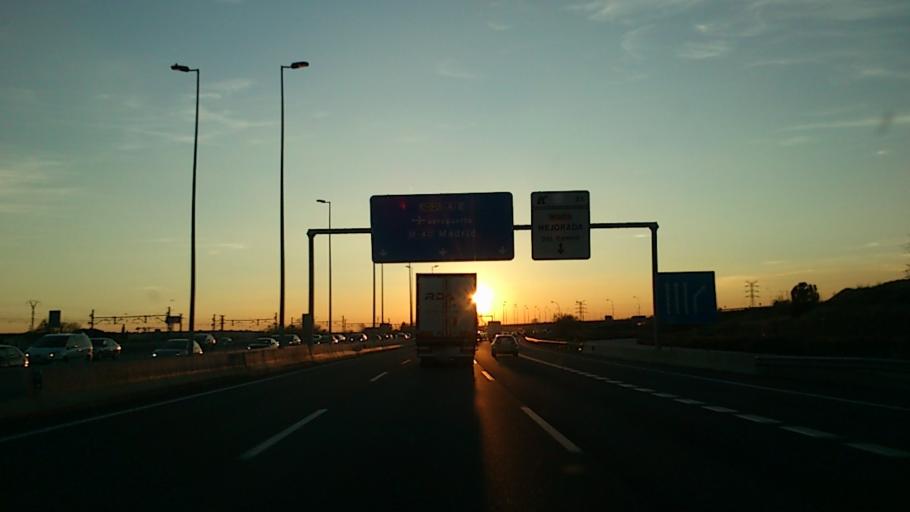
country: ES
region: Madrid
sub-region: Provincia de Madrid
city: Alcala de Henares
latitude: 40.4763
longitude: -3.4085
